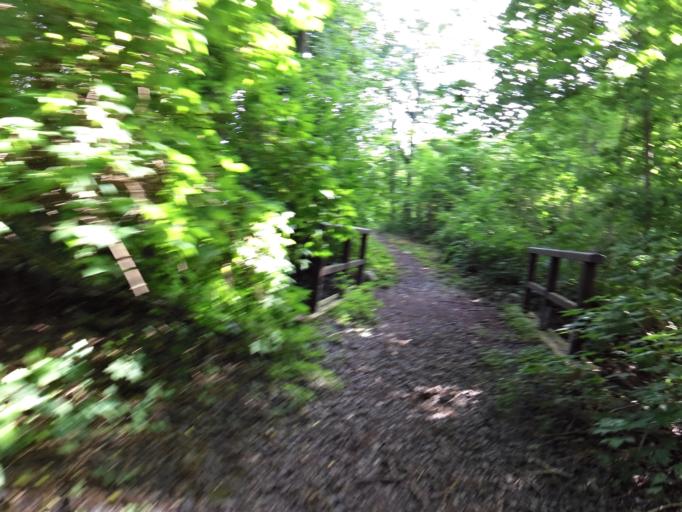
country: DE
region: Saxony
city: Markkleeberg
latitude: 51.2890
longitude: 12.4251
